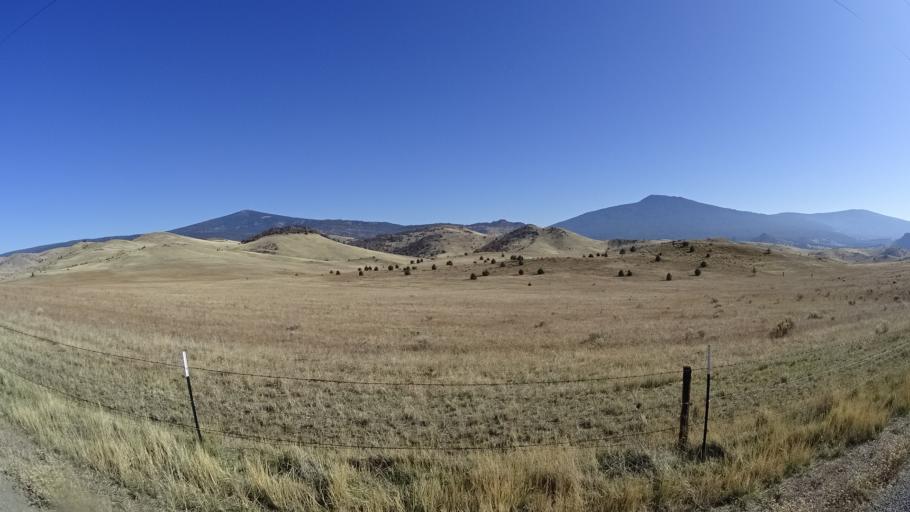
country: US
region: California
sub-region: Siskiyou County
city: Montague
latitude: 41.7723
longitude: -122.3591
